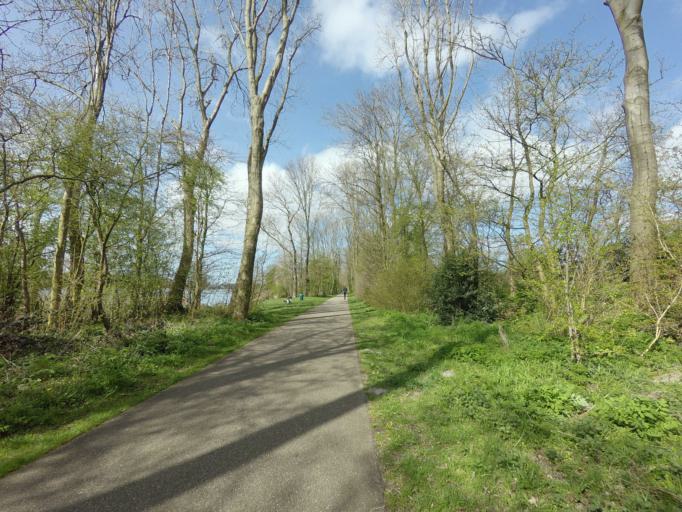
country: NL
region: Utrecht
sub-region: Stichtse Vecht
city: Maarssen
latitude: 52.1405
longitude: 5.0940
